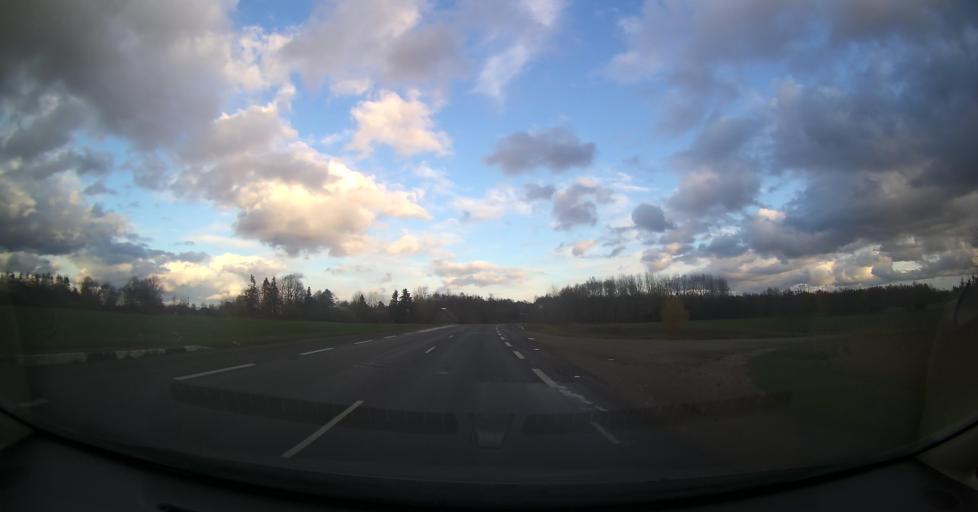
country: EE
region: Harju
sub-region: Raasiku vald
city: Arukula
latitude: 59.3439
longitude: 25.1195
